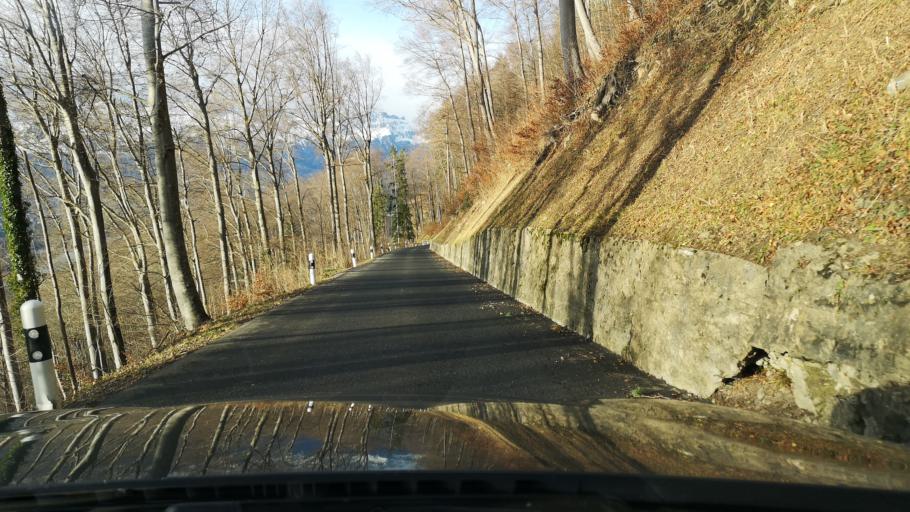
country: LI
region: Triesenberg
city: Triesenberg
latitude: 47.1279
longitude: 9.5321
